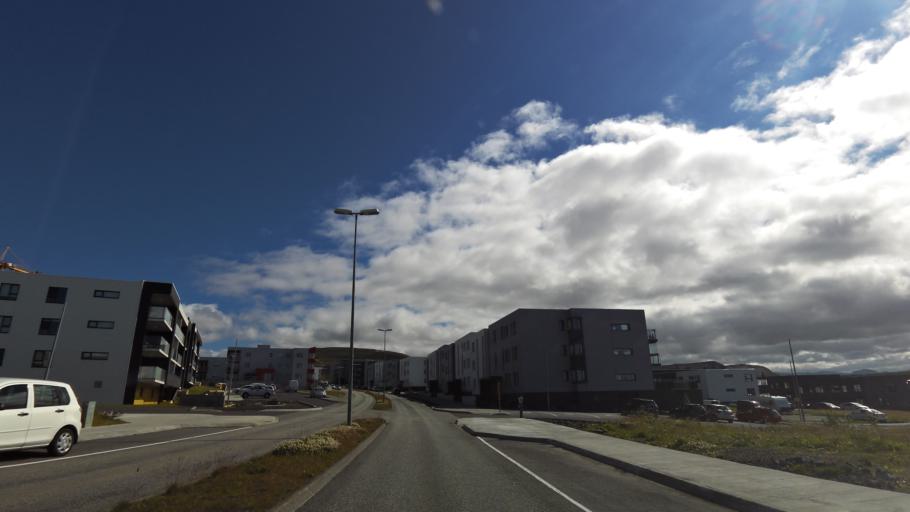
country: IS
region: Capital Region
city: Mosfellsbaer
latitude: 64.1687
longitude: -21.6712
